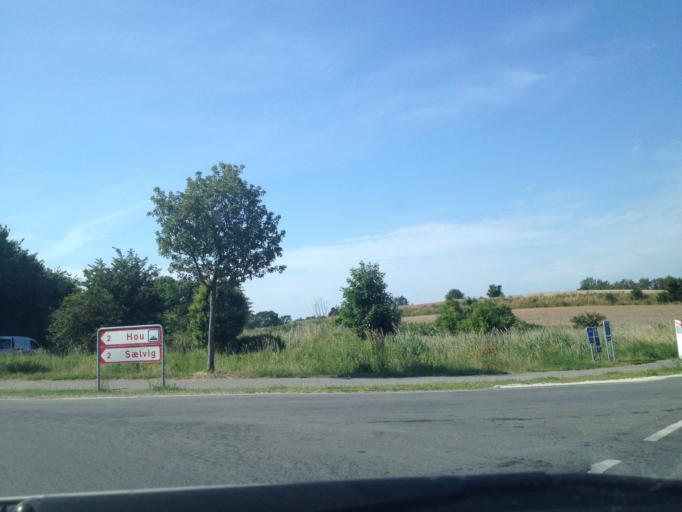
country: DK
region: Central Jutland
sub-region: Samso Kommune
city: Tranebjerg
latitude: 55.8595
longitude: 10.5718
